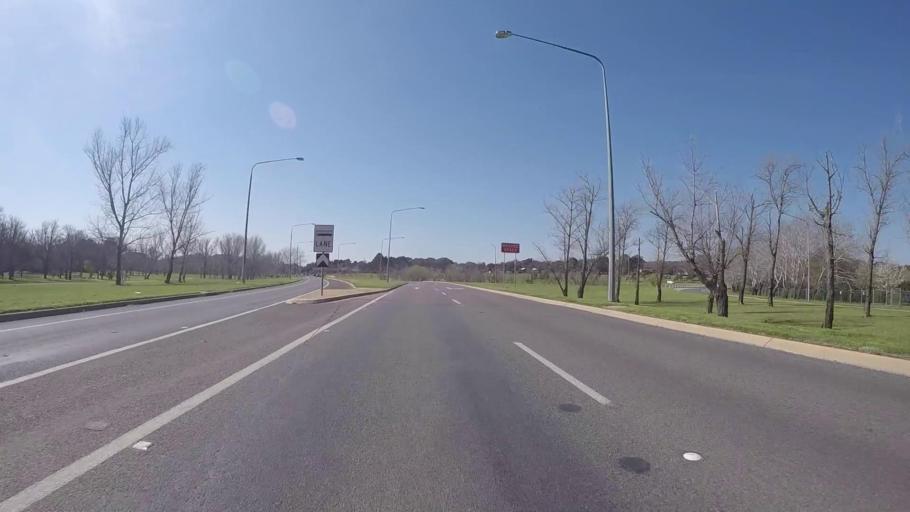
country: AU
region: Australian Capital Territory
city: Forrest
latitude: -35.3372
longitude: 149.0849
